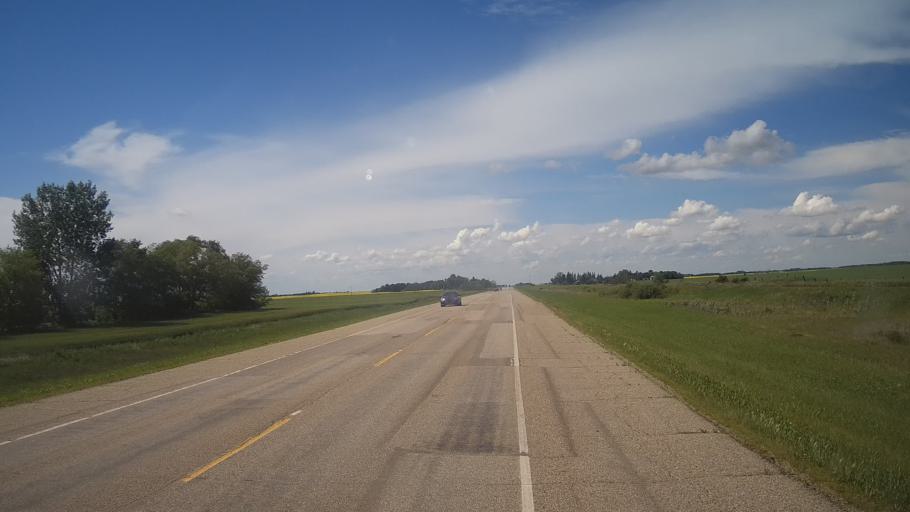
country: CA
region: Saskatchewan
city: Yorkton
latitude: 51.0856
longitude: -102.2535
